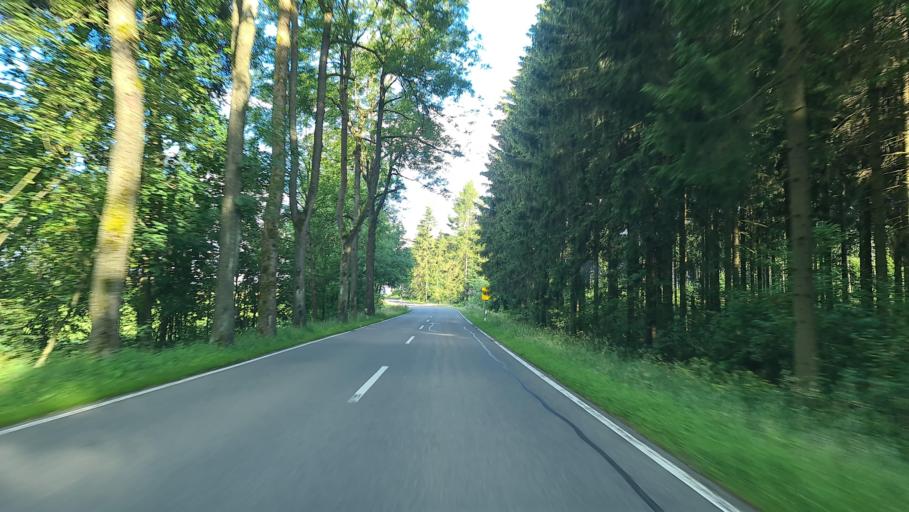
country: DE
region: Saxony
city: Pfaffroda
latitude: 50.7304
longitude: 13.3812
